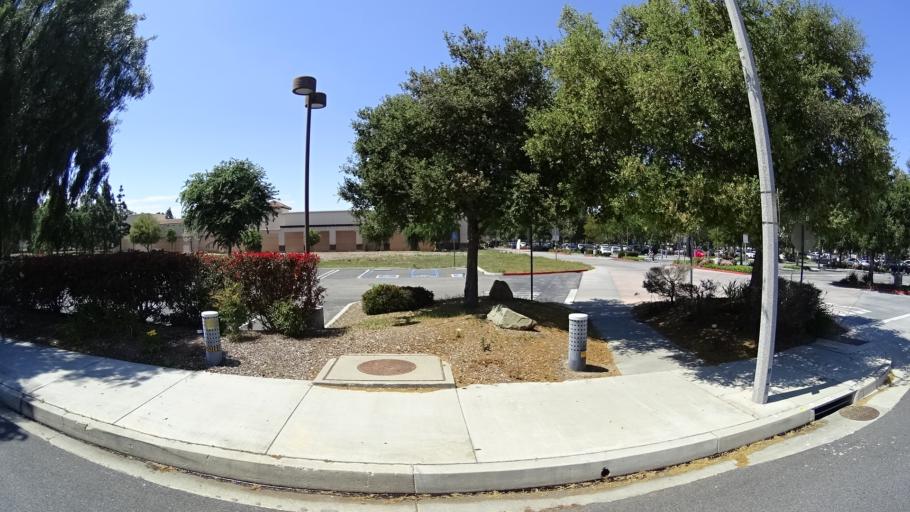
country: US
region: California
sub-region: Ventura County
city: Casa Conejo
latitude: 34.1825
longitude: -118.9211
